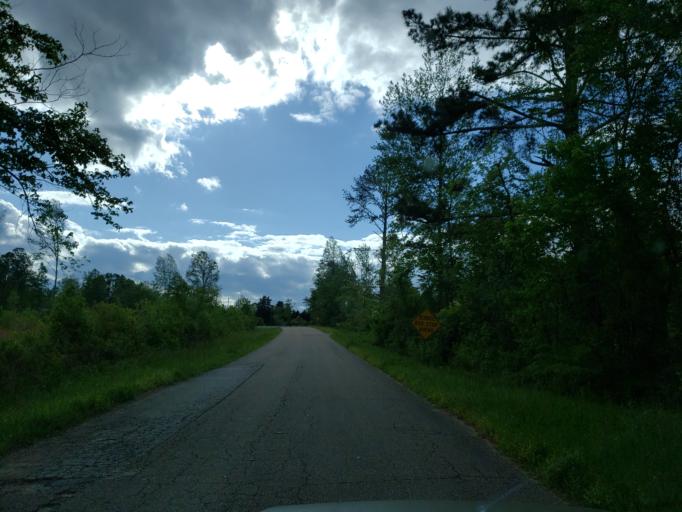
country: US
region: Georgia
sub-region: Haralson County
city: Tallapoosa
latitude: 33.7746
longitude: -85.3773
